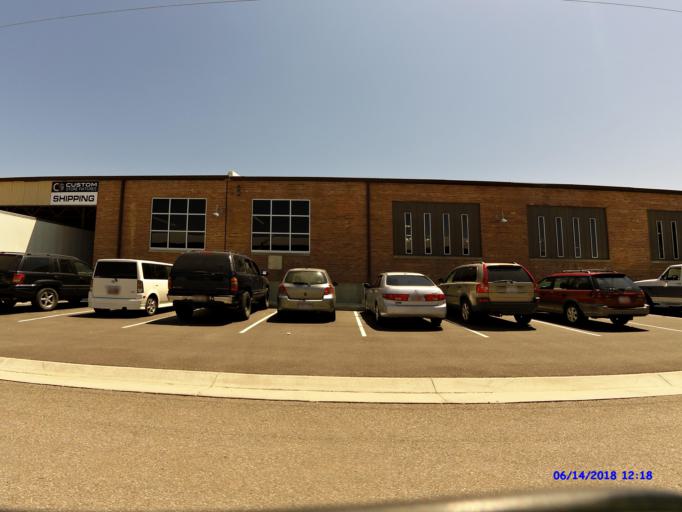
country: US
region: Utah
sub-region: Weber County
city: Harrisville
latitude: 41.2620
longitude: -111.9965
